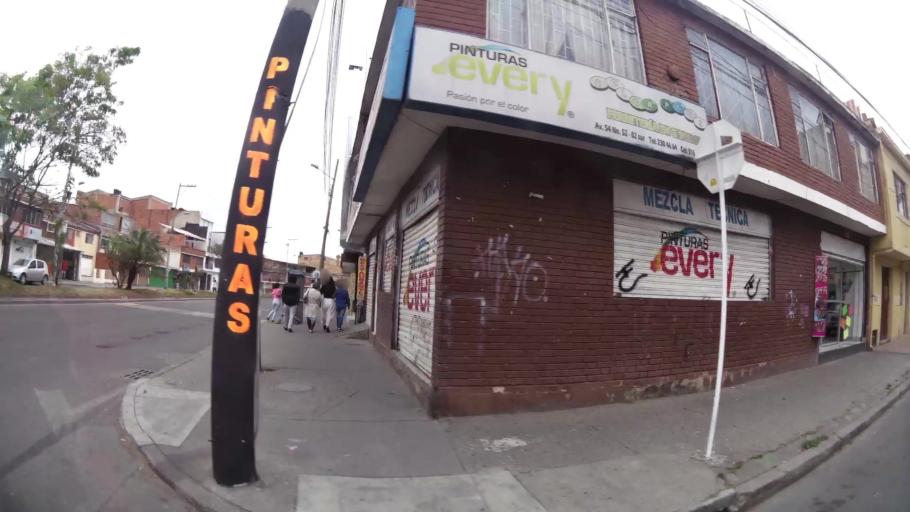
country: CO
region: Bogota D.C.
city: Bogota
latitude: 4.5886
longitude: -74.1417
